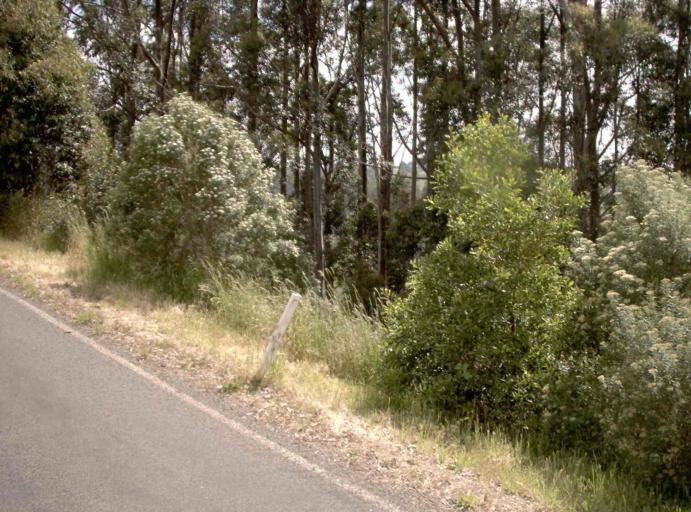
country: AU
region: Victoria
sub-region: Latrobe
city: Traralgon
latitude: -38.3481
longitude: 146.5683
